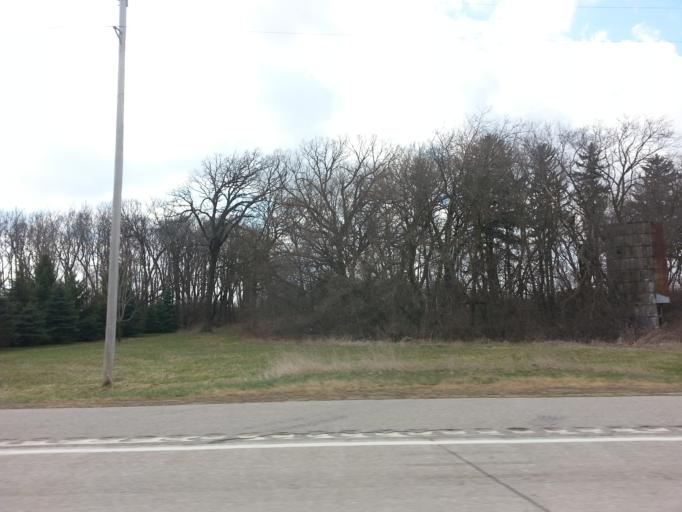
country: US
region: Minnesota
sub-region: Olmsted County
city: Byron
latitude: 44.0932
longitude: -92.6783
